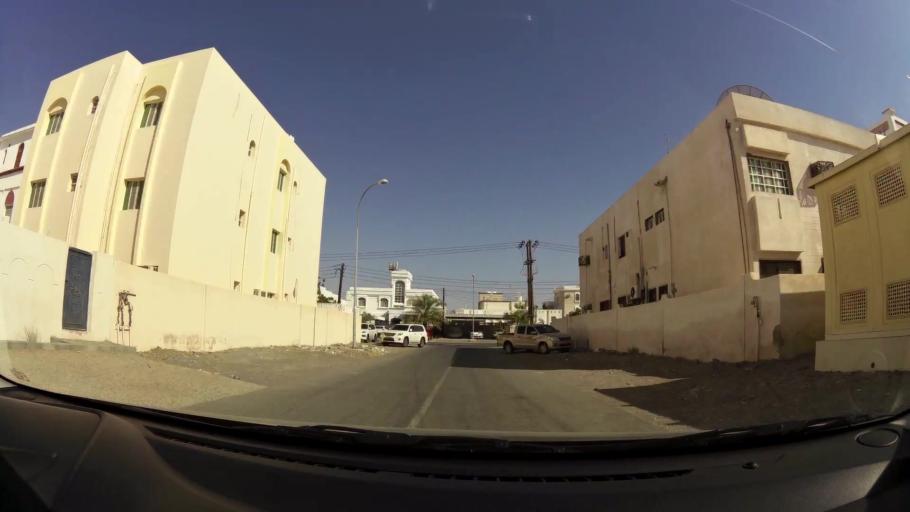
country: OM
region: Muhafazat Masqat
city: As Sib al Jadidah
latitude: 23.6305
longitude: 58.2038
